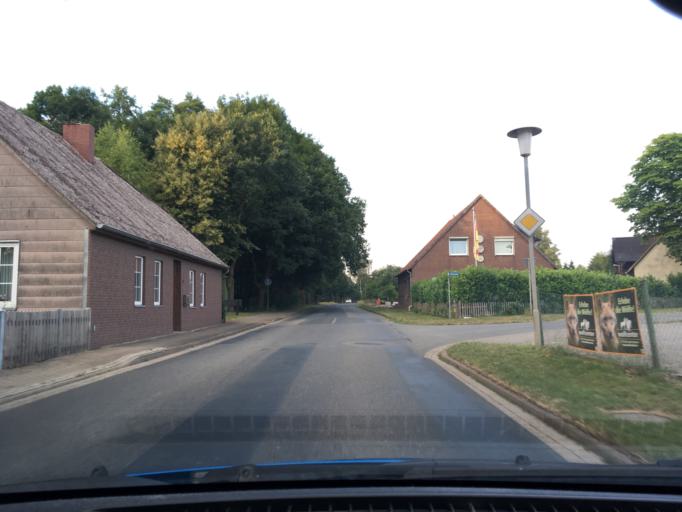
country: DE
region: Lower Saxony
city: Steinhorst
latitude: 52.6901
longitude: 10.4109
